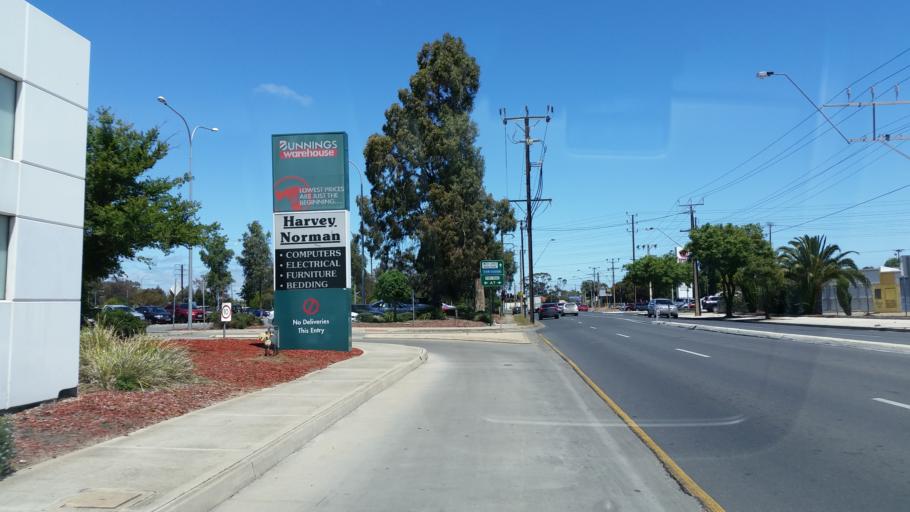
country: AU
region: South Australia
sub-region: Charles Sturt
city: Albert Park
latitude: -34.8744
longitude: 138.5284
